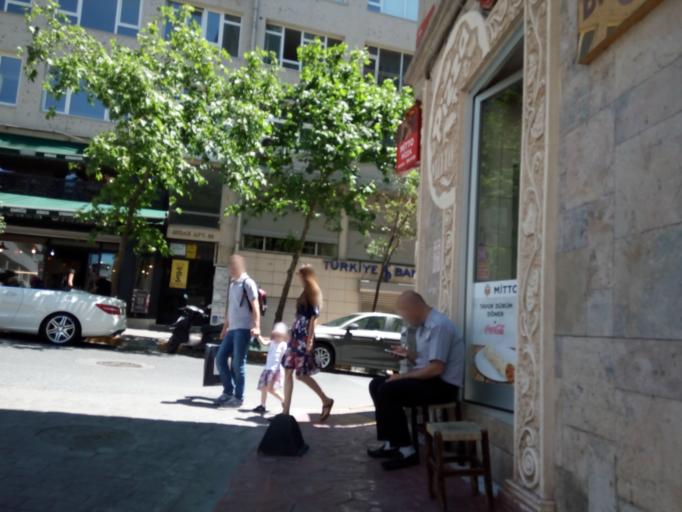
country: TR
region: Istanbul
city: Eminoenue
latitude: 41.0325
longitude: 28.9833
